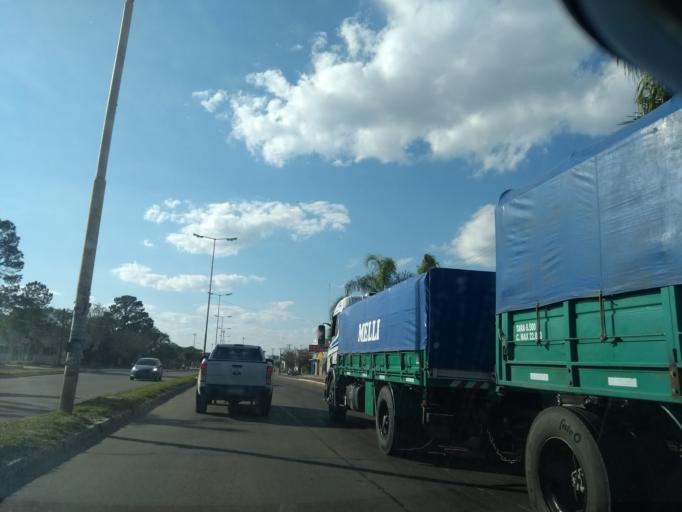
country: AR
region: Corrientes
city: Corrientes
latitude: -27.4840
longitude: -58.7877
